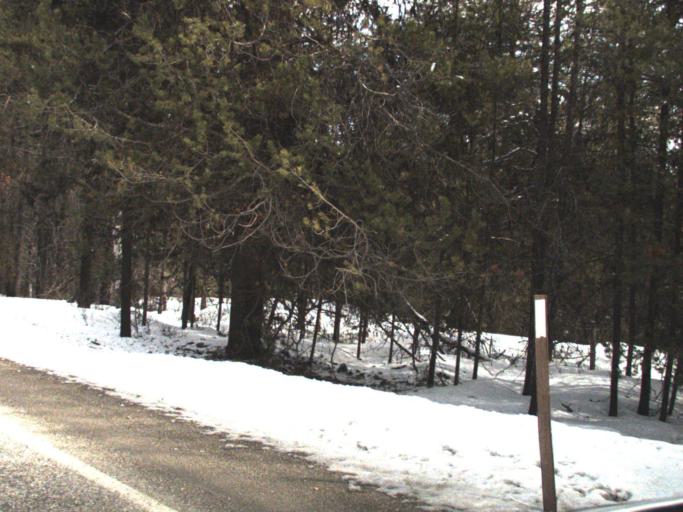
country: US
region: Washington
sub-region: Stevens County
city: Colville
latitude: 48.6596
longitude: -117.4764
